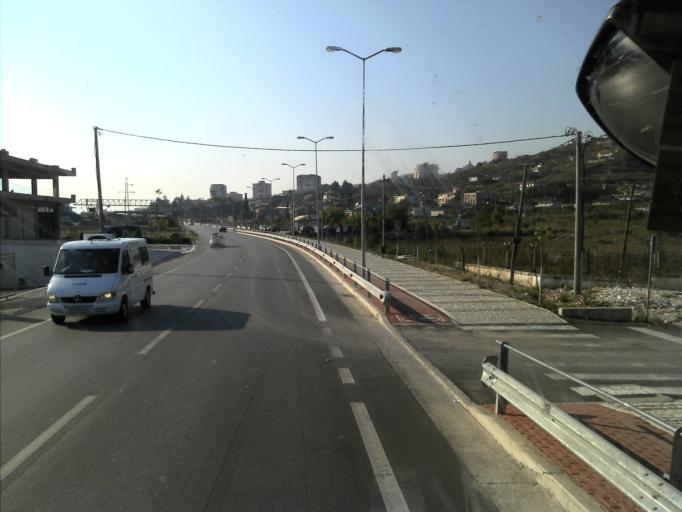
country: AL
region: Gjirokaster
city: Gjirokaster
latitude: 40.0911
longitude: 20.1373
